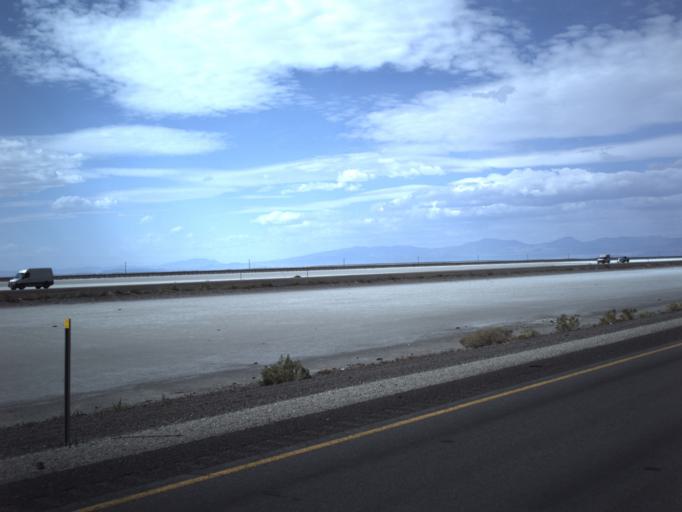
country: US
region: Utah
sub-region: Tooele County
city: Wendover
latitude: 40.7359
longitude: -113.6841
